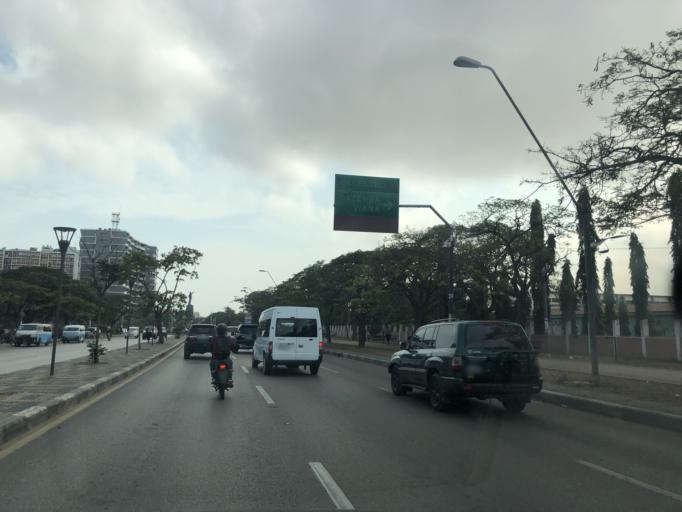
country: AO
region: Luanda
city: Luanda
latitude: -8.8289
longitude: 13.2427
